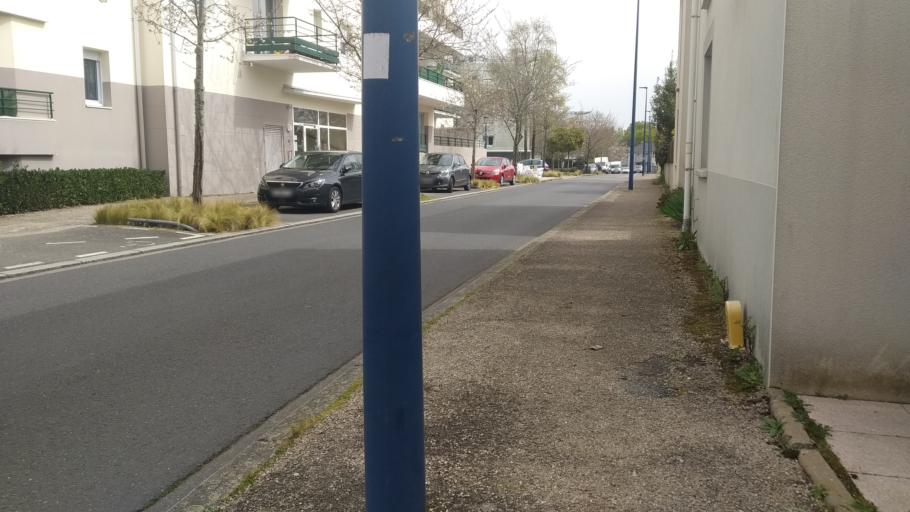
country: FR
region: Pays de la Loire
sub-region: Departement de la Loire-Atlantique
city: Sainte-Luce-sur-Loire
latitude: 47.2461
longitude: -1.5143
